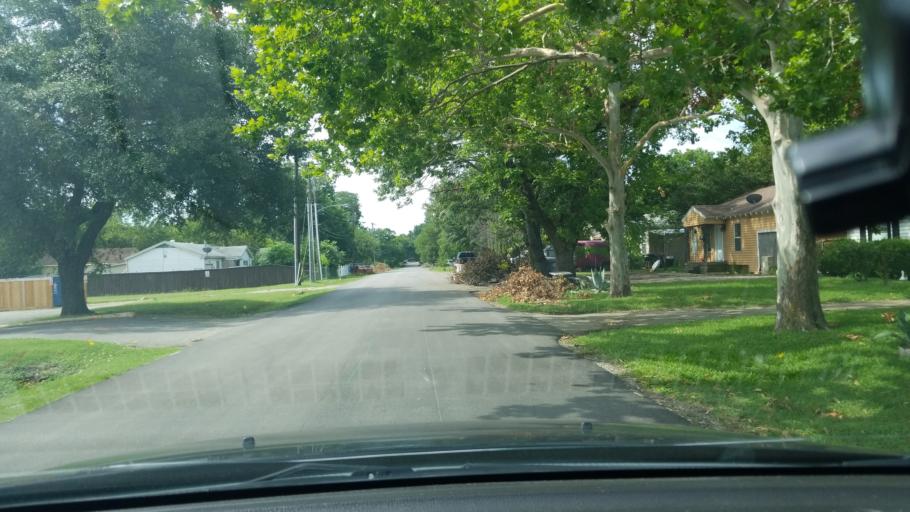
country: US
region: Texas
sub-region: Dallas County
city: Balch Springs
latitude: 32.7673
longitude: -96.6749
